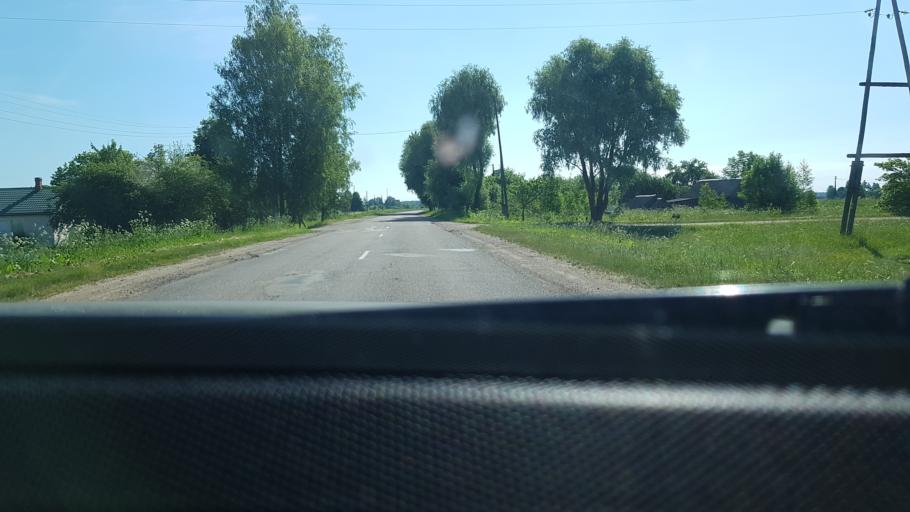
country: LV
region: Daugavpils
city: Daugavpils
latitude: 55.8219
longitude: 26.7752
